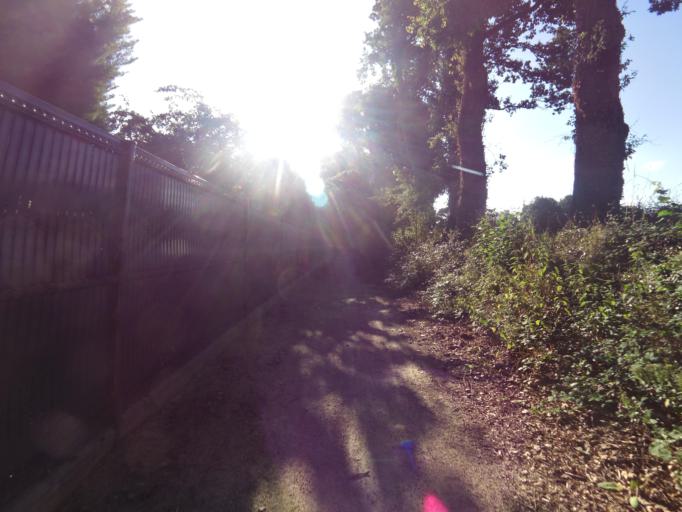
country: FR
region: Brittany
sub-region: Departement du Morbihan
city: Ploermel
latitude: 47.9260
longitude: -2.4080
